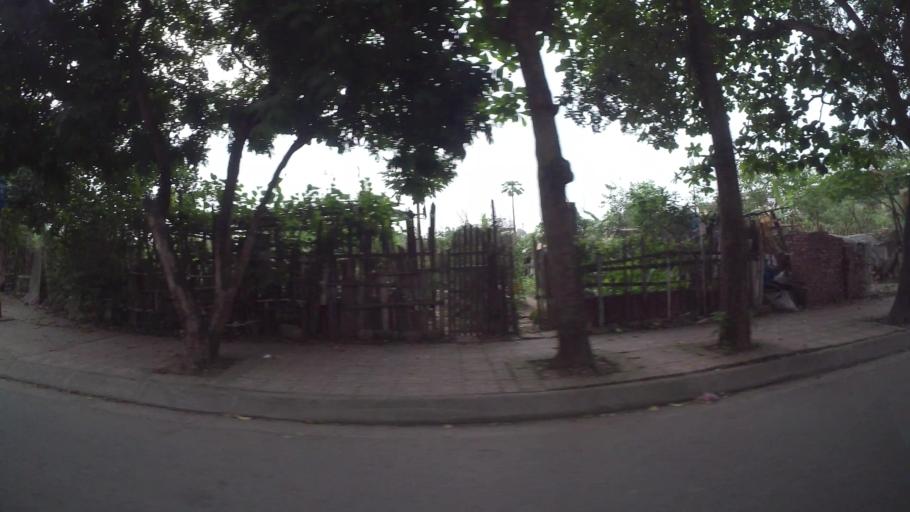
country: VN
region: Ha Noi
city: Hoan Kiem
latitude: 21.0663
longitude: 105.8825
